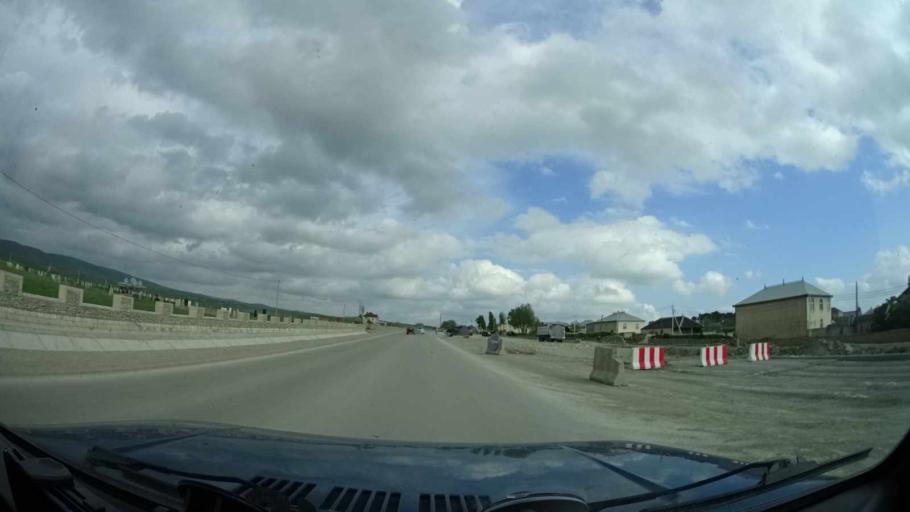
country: AZ
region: Samaxi
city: Shamakhi
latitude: 40.5917
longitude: 48.7047
